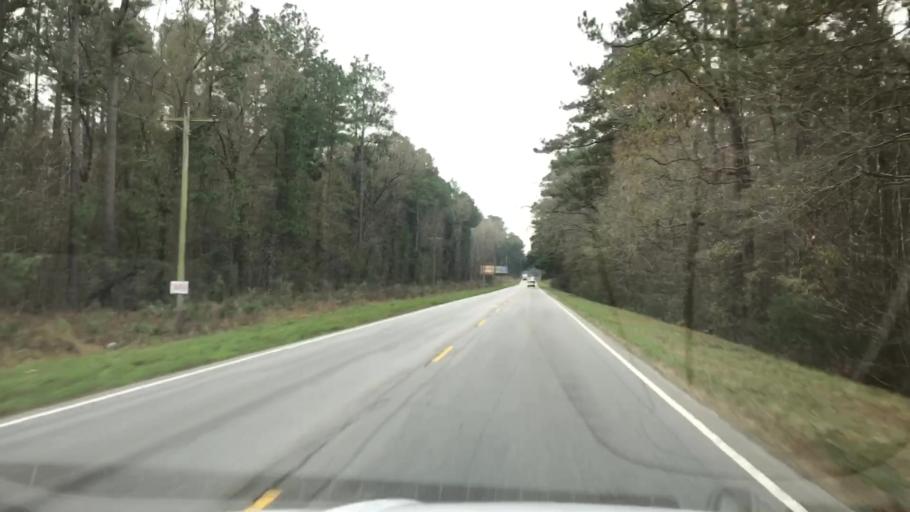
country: US
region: South Carolina
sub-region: Jasper County
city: Ridgeland
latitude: 32.4008
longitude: -80.9065
